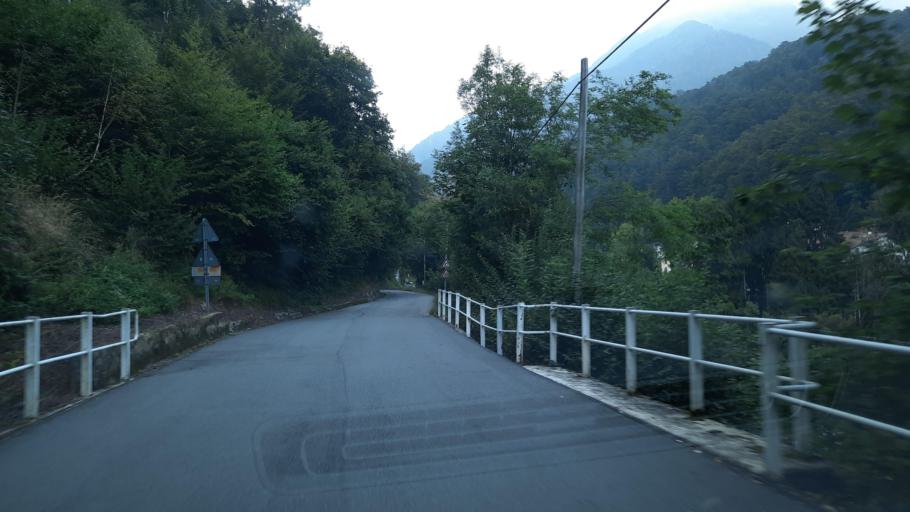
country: IT
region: Piedmont
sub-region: Provincia di Biella
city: Campiglia Cervo
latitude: 45.6618
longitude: 7.9975
